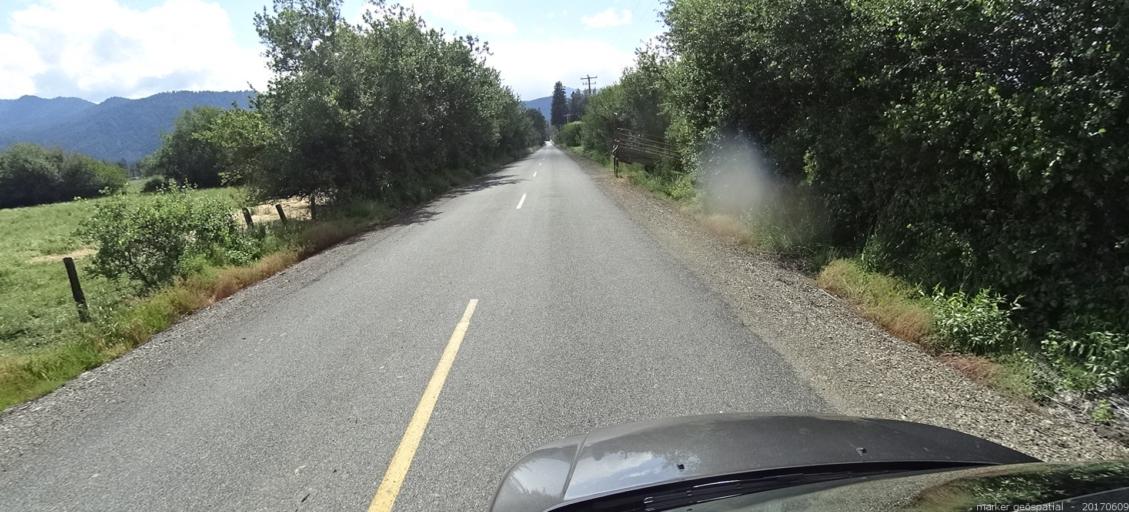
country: US
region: California
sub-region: Siskiyou County
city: Yreka
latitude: 41.5152
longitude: -122.8938
